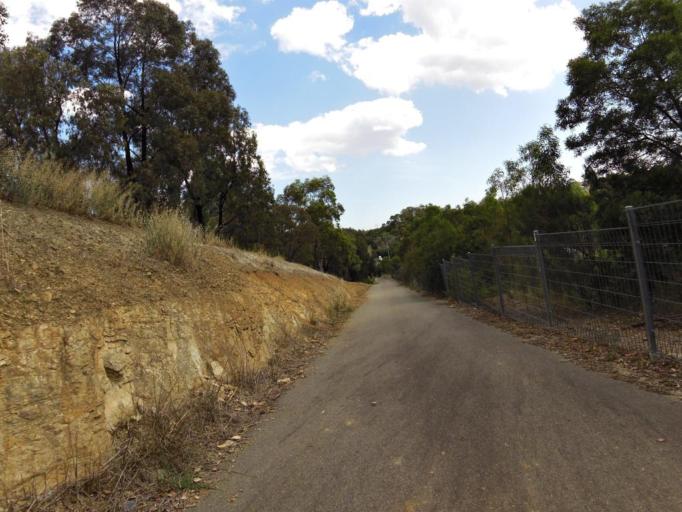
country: AU
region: Victoria
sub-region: Banyule
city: Watsonia North
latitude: -37.6955
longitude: 145.0927
